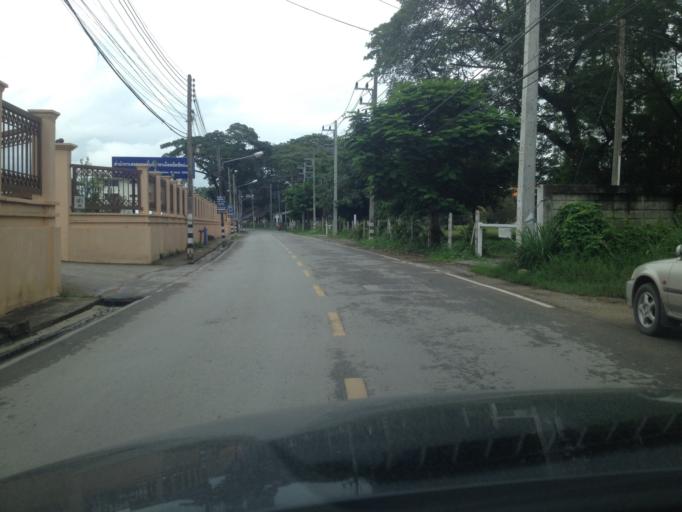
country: TH
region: Chiang Mai
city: Chiang Mai
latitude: 18.7642
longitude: 99.0020
